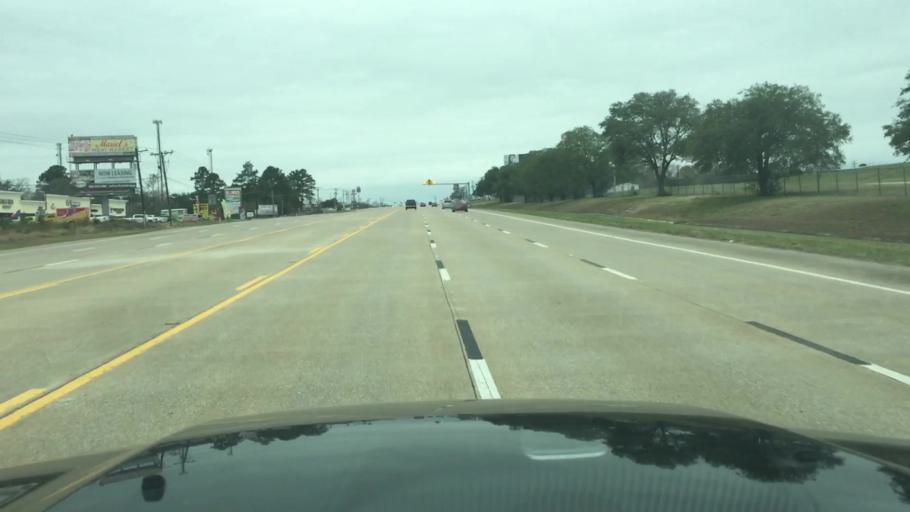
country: US
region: Texas
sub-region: Montgomery County
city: Panorama Village
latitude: 30.3517
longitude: -95.5766
